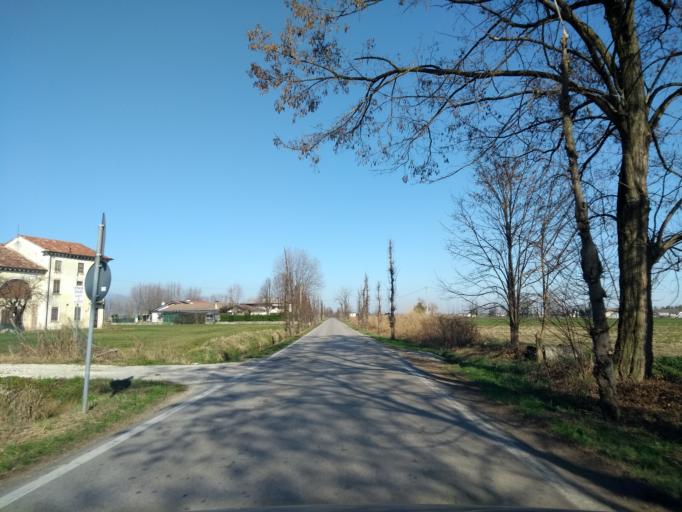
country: IT
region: Veneto
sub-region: Provincia di Padova
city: San Pietro in Gu
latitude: 45.6152
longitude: 11.6511
